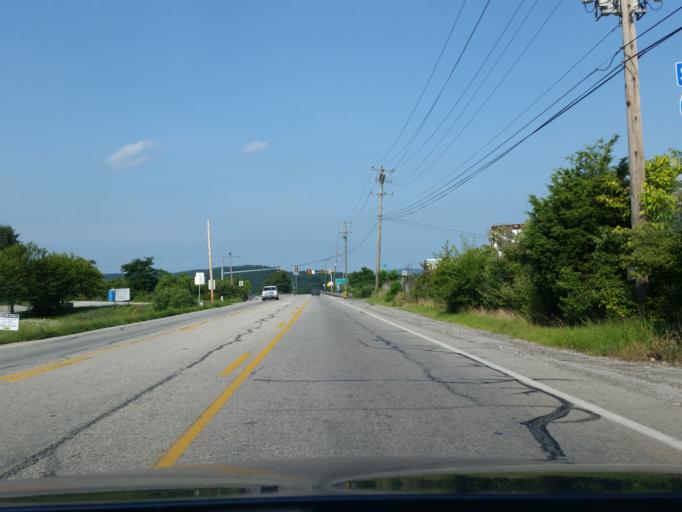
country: US
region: Pennsylvania
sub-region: York County
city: Emigsville
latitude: 40.0199
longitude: -76.7459
